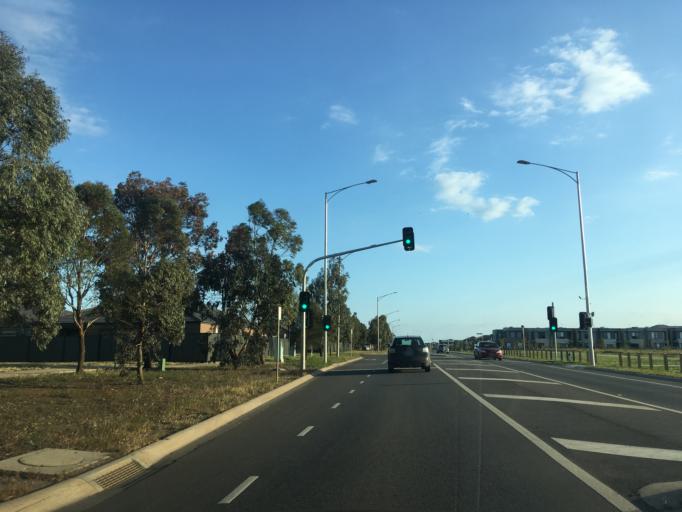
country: AU
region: Victoria
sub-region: Wyndham
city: Hoppers Crossing
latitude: -37.8884
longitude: 144.7182
